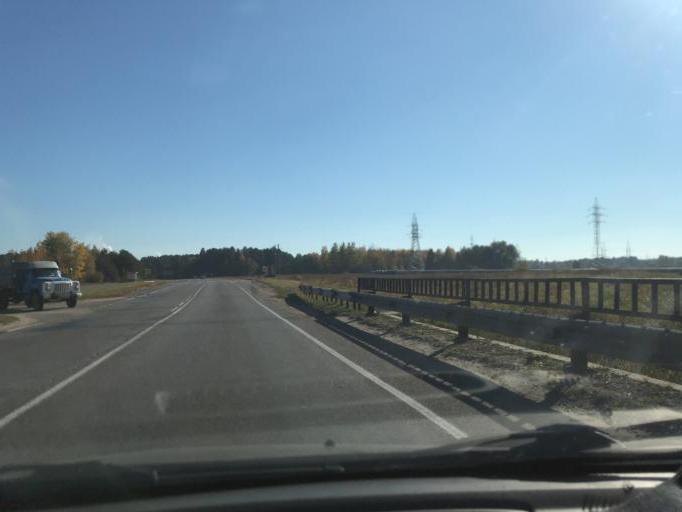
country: BY
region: Gomel
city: Kastsyukowka
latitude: 52.4514
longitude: 30.8266
